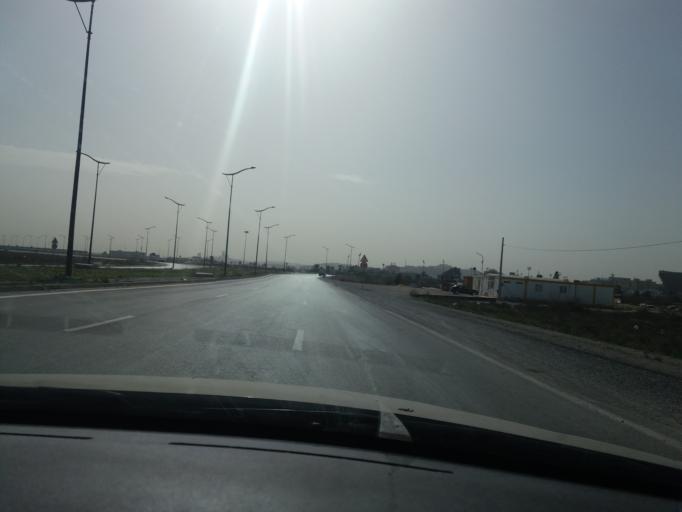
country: TN
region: Tunis
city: Tunis
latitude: 36.8090
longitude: 10.1929
